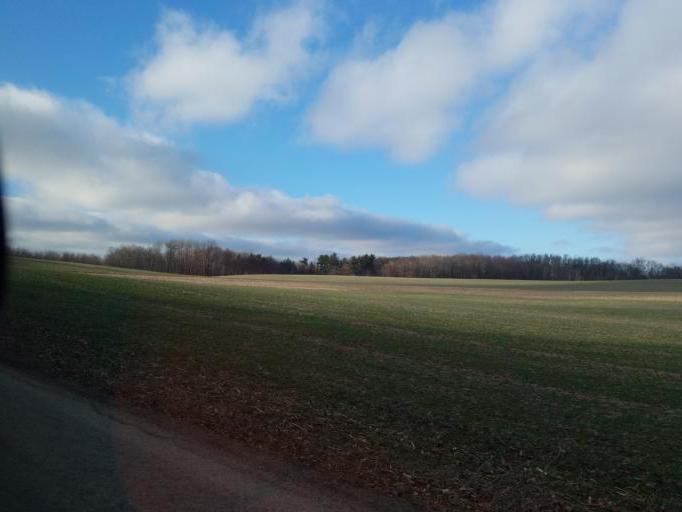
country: US
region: Ohio
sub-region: Ashland County
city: Loudonville
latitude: 40.6091
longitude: -82.3663
